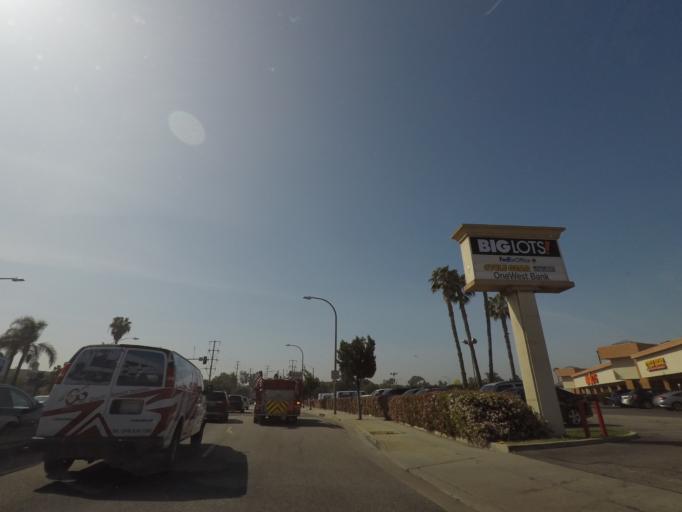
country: US
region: California
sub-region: Los Angeles County
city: Ladera Heights
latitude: 33.9911
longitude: -118.3953
